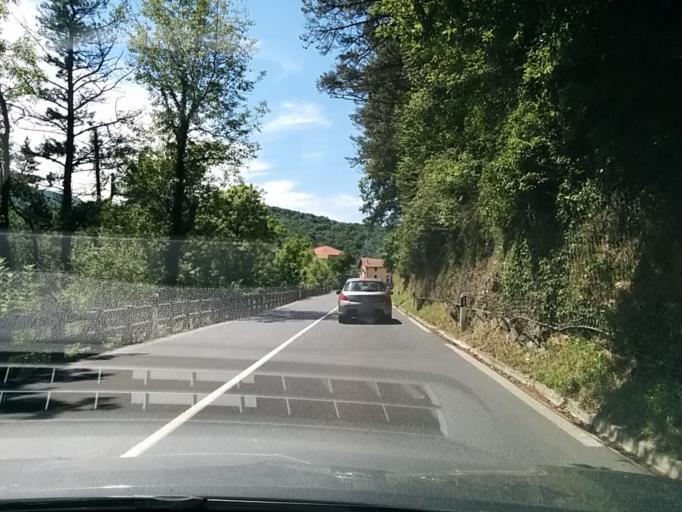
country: ES
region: Basque Country
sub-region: Provincia de Guipuzcoa
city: Usurbil
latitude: 43.2809
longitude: -2.0816
